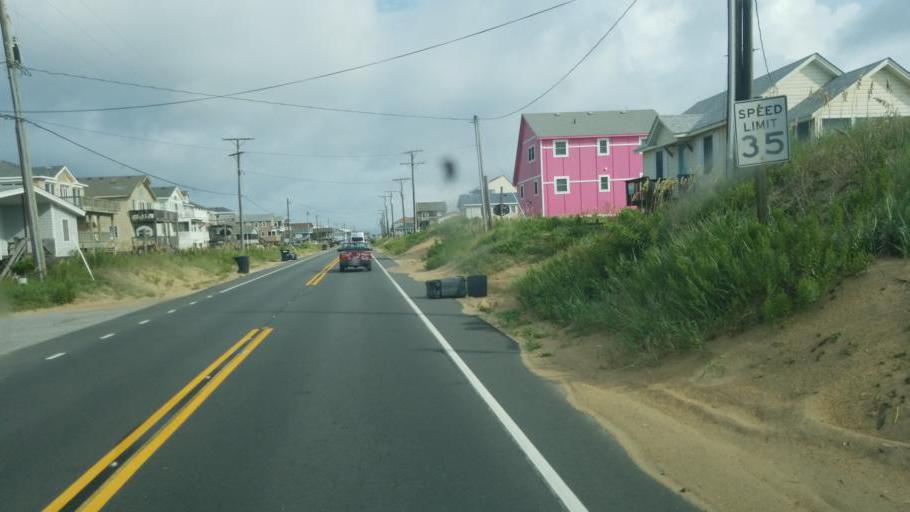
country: US
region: North Carolina
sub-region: Dare County
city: Kitty Hawk
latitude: 36.0756
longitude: -75.6963
